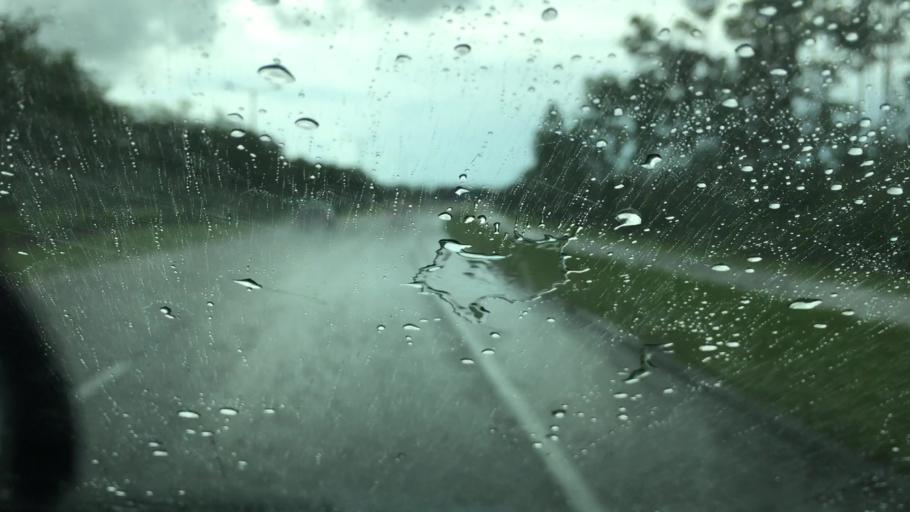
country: US
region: Florida
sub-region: Lee County
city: Three Oaks
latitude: 26.4591
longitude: -81.7828
